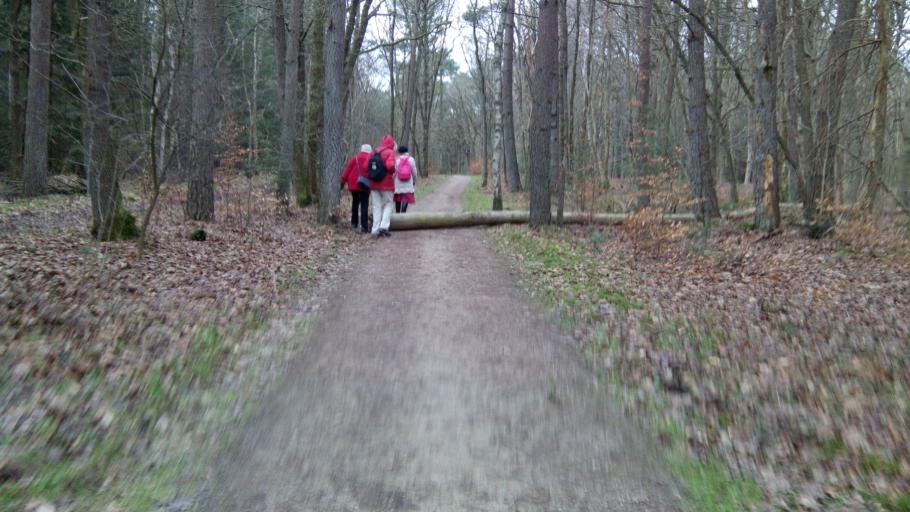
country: NL
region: North Holland
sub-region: Gemeente Hilversum
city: Hilversum
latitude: 52.1975
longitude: 5.2074
